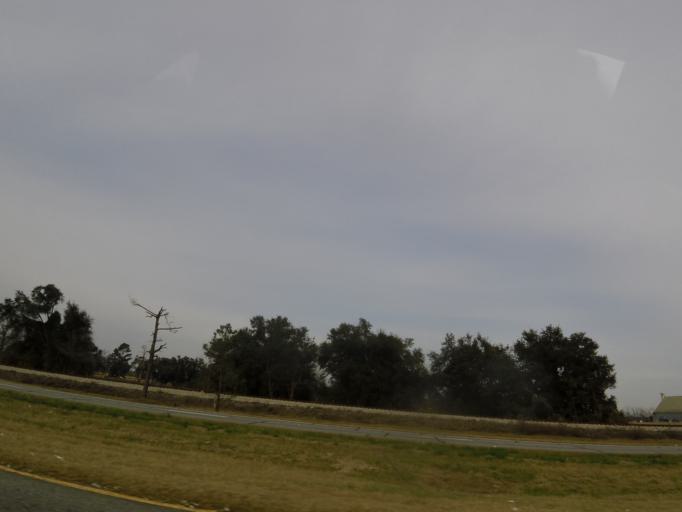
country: US
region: Georgia
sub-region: Seminole County
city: Donalsonville
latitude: 31.0315
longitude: -84.8558
